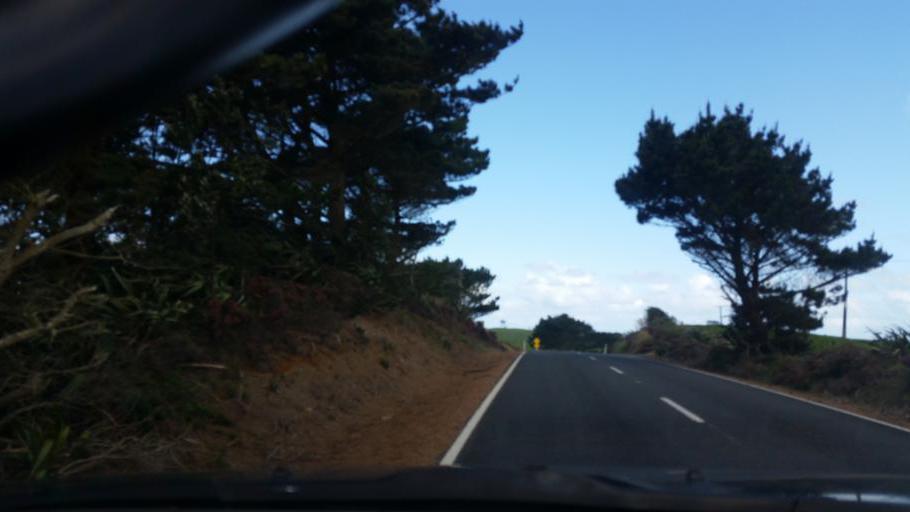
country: NZ
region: Northland
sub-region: Kaipara District
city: Dargaville
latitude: -36.0616
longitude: 173.8686
